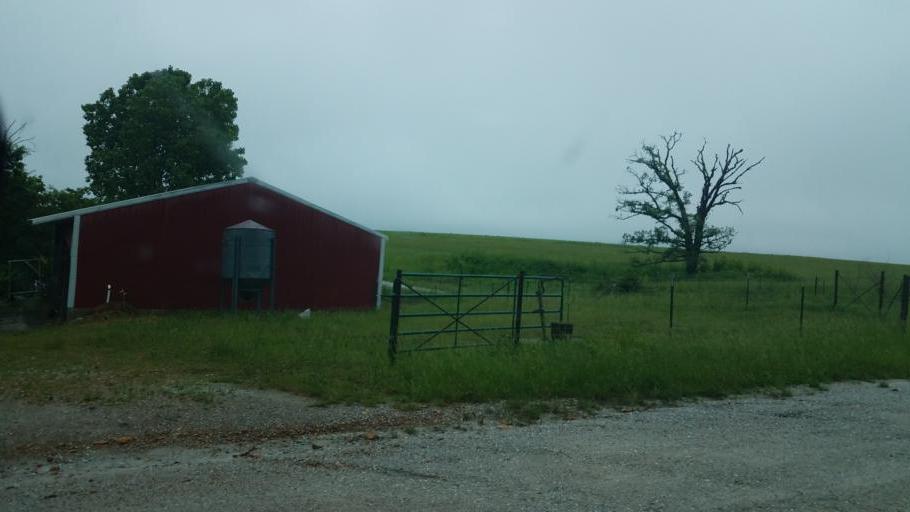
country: US
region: Missouri
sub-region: Moniteau County
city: California
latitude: 38.7597
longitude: -92.6061
